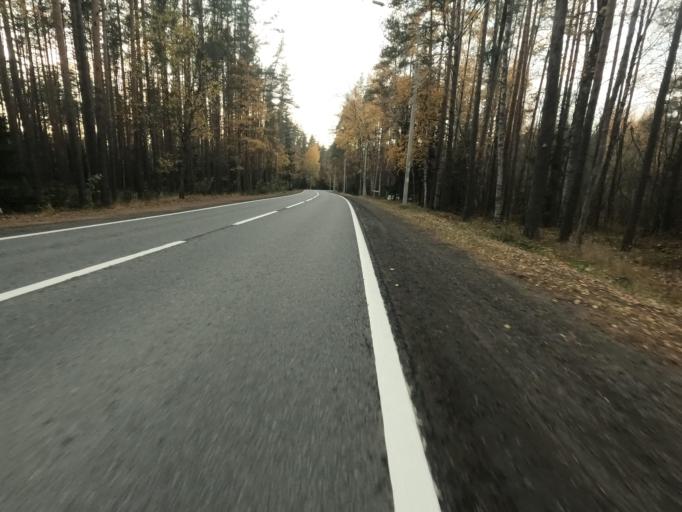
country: RU
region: St.-Petersburg
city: Repino
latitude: 60.1910
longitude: 29.8605
